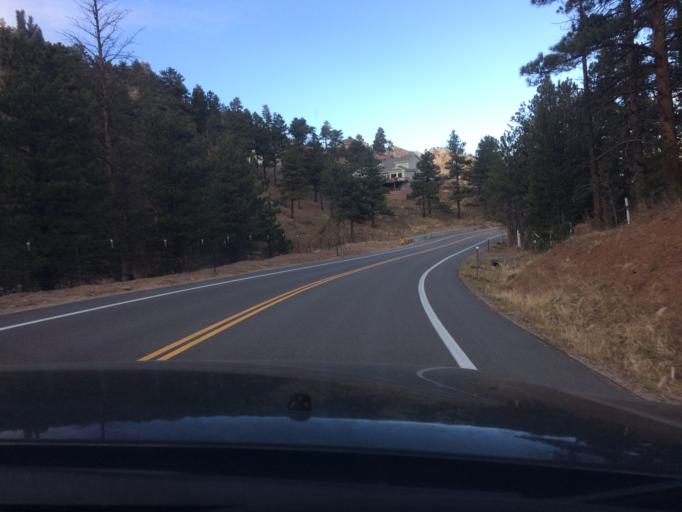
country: US
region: Colorado
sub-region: Boulder County
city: Boulder
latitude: 40.1141
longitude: -105.3078
